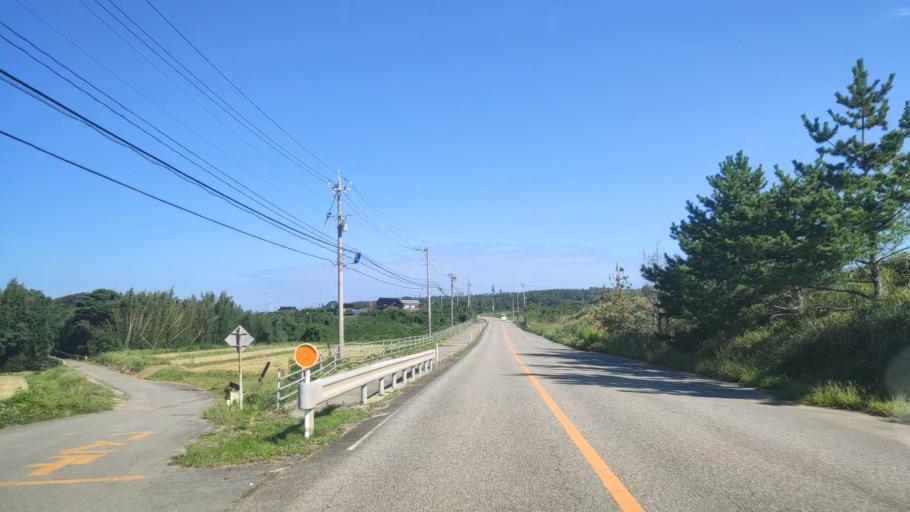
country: JP
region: Ishikawa
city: Hakui
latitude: 37.0318
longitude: 136.7472
